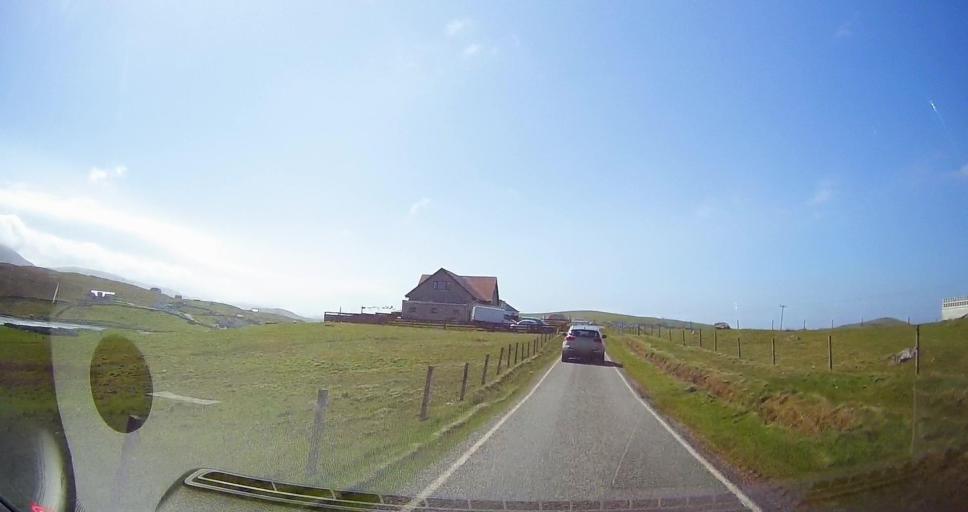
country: GB
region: Scotland
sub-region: Shetland Islands
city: Sandwick
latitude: 60.0861
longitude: -1.3309
